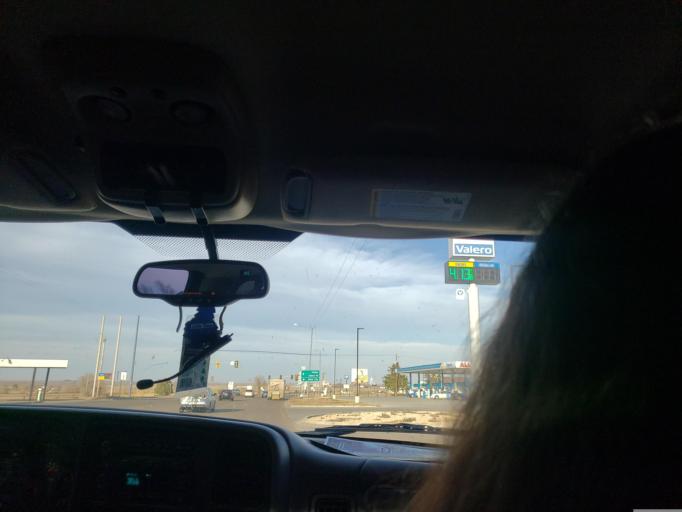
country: US
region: Oklahoma
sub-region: Texas County
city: Guymon
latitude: 36.6881
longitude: -101.4666
